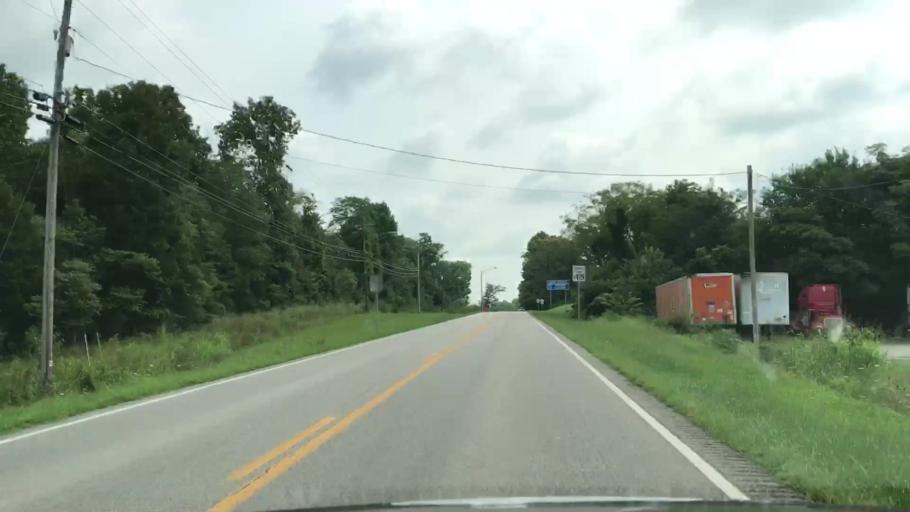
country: US
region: Kentucky
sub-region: Barren County
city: Cave City
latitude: 37.0921
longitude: -86.0573
